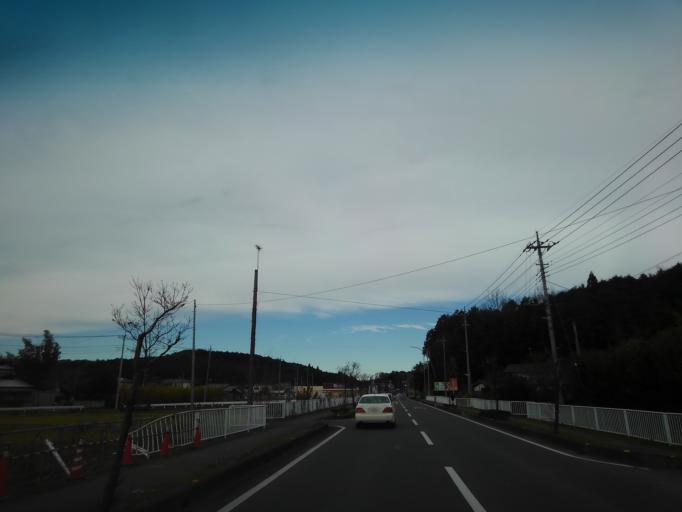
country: JP
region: Saitama
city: Morohongo
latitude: 35.9677
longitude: 139.3020
